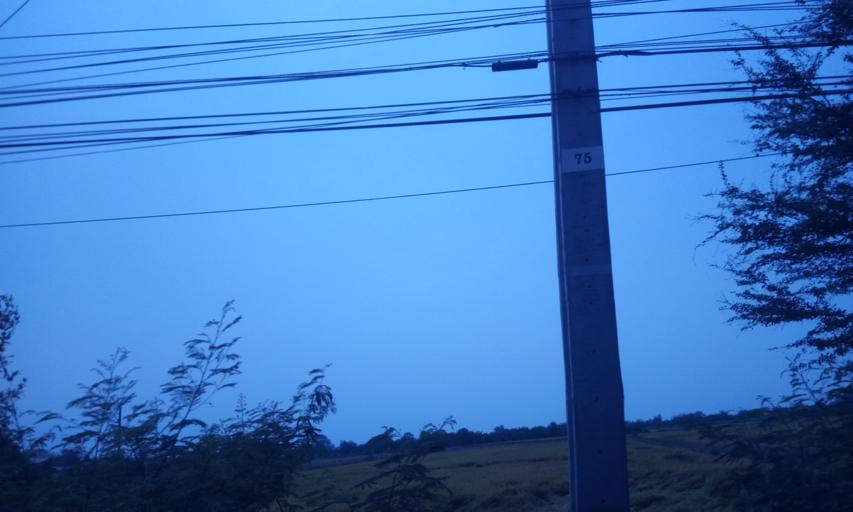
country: TH
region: Nonthaburi
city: Sai Noi
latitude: 13.9469
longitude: 100.3139
